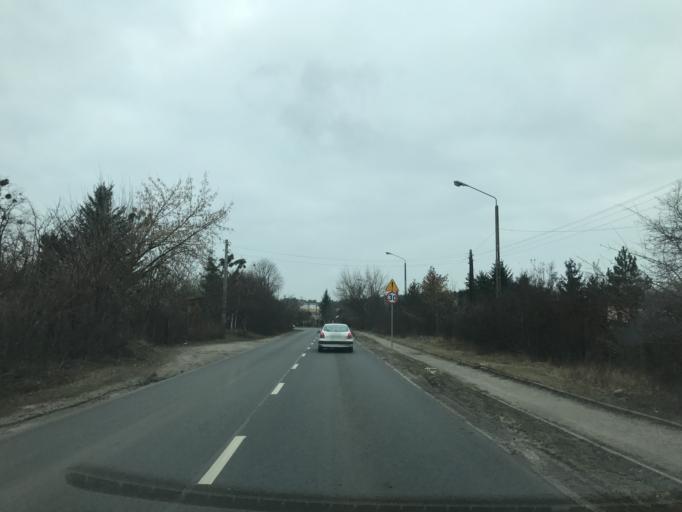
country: PL
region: Kujawsko-Pomorskie
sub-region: Bydgoszcz
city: Bydgoszcz
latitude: 53.1040
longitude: 18.0641
